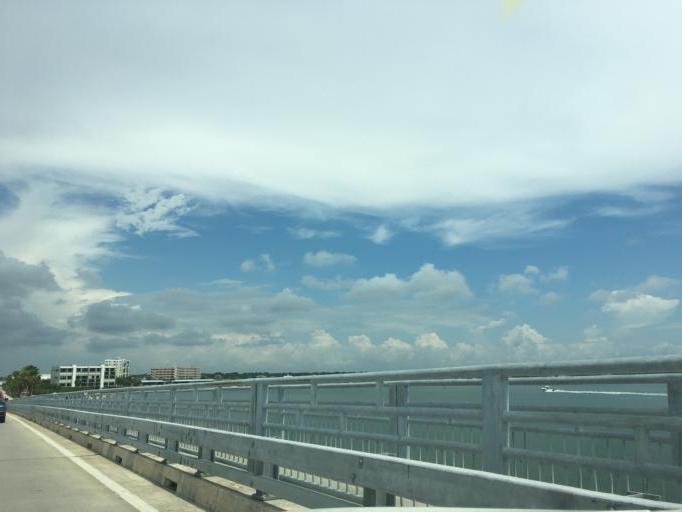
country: US
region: Florida
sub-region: Pinellas County
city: Dunedin
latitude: 28.0511
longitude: -82.7948
